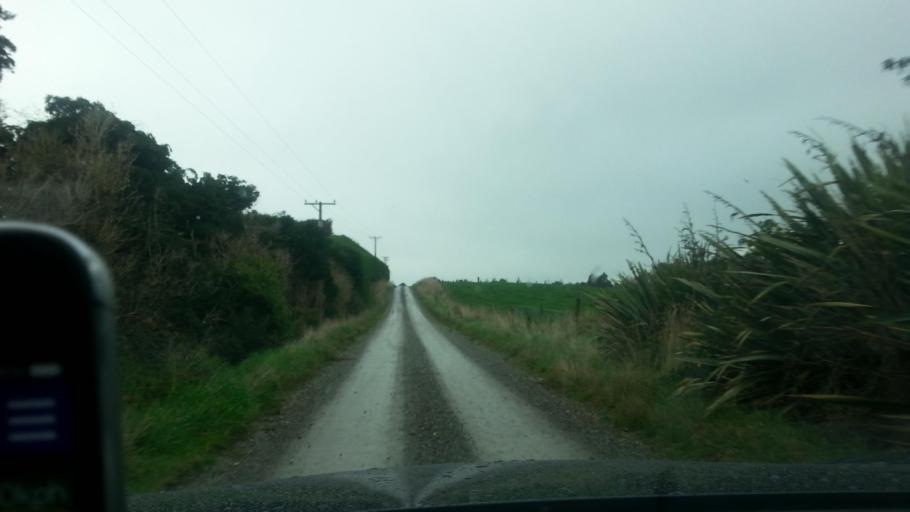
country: NZ
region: Southland
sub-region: Invercargill City
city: Invercargill
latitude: -46.3387
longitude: 168.4051
